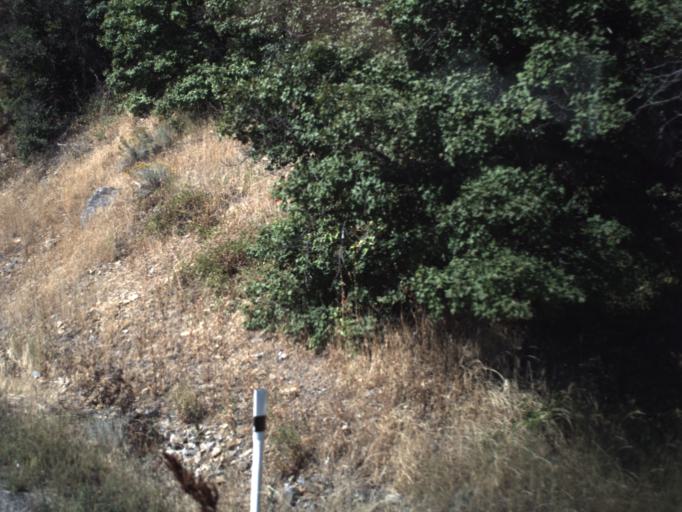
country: US
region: Utah
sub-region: Cache County
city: Millville
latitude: 41.6211
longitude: -111.7592
